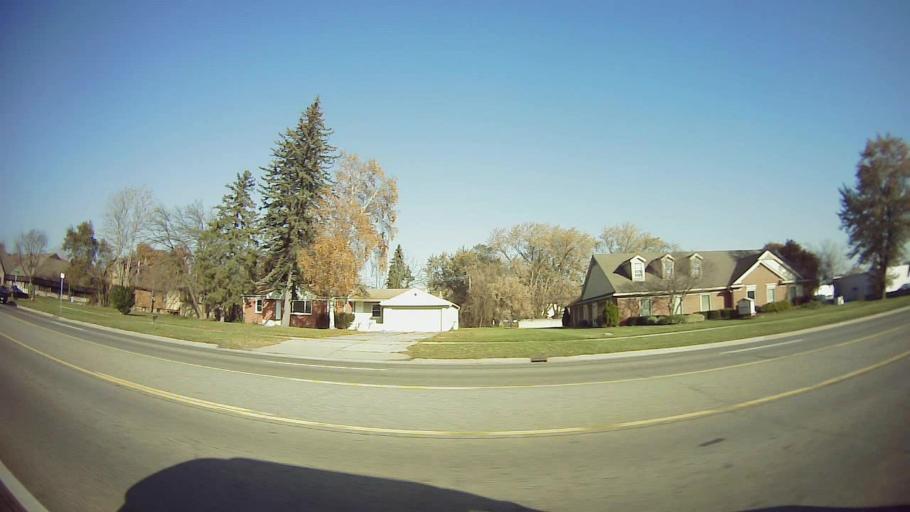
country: US
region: Michigan
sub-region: Oakland County
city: Clawson
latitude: 42.5486
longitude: -83.1337
